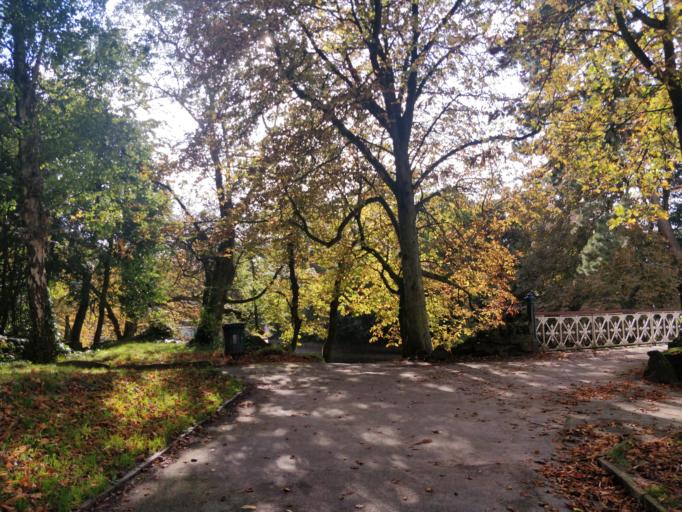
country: GB
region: England
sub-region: Lancashire
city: Banks
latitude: 53.6607
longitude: -2.9586
